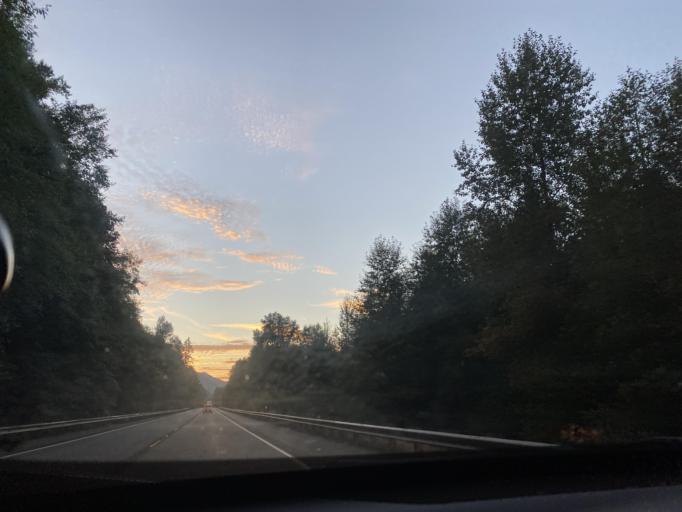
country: US
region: Washington
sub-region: Clallam County
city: Port Angeles
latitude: 48.0718
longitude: -123.6420
